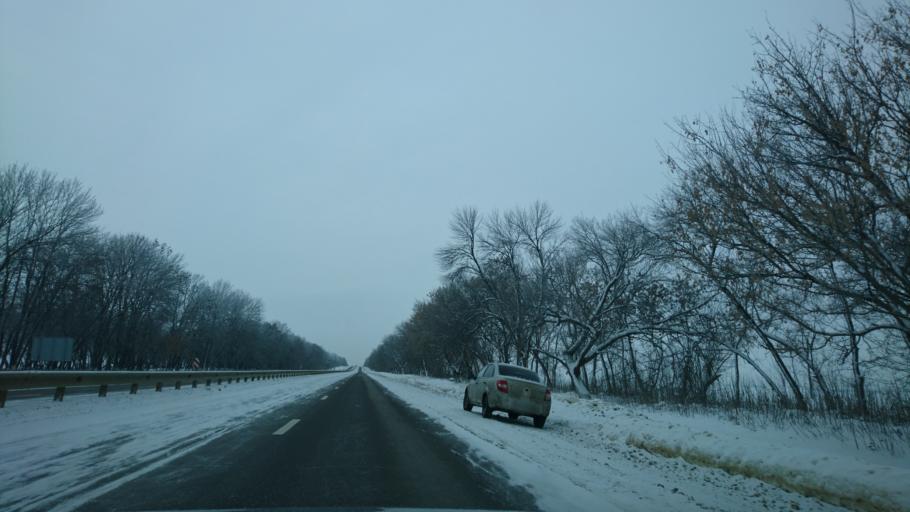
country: RU
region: Belgorod
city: Mayskiy
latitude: 50.4276
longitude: 36.3831
